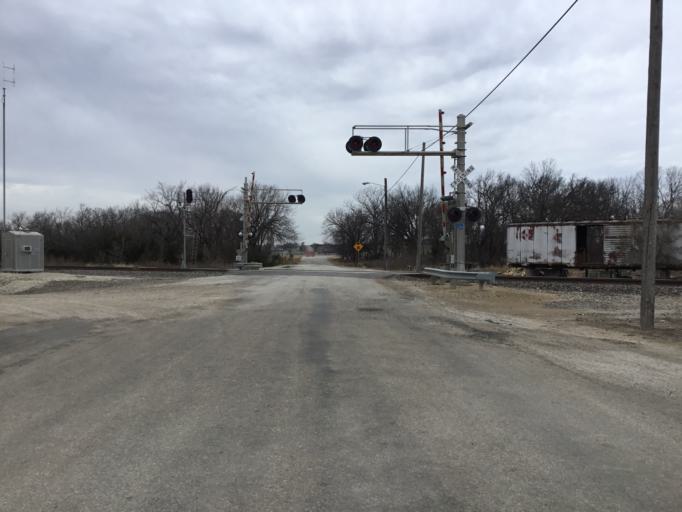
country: US
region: Kansas
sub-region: Chase County
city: Cottonwood Falls
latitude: 38.3735
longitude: -96.6473
